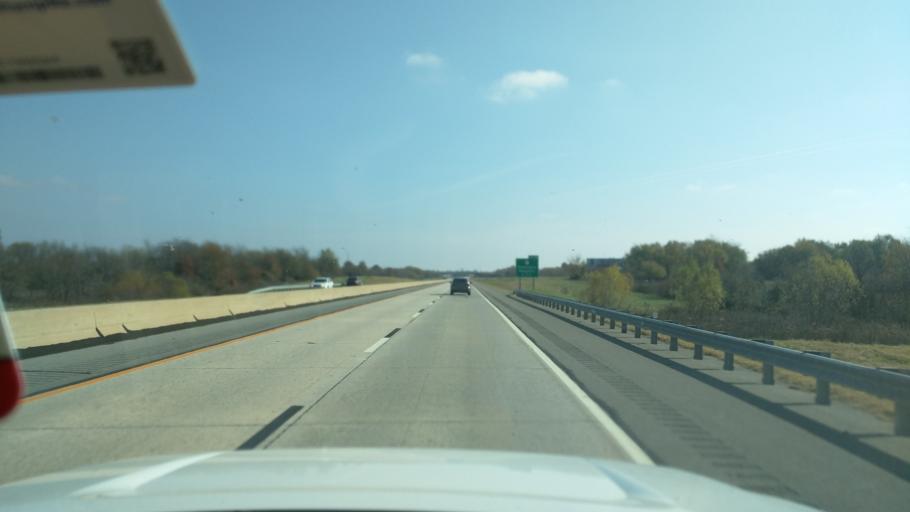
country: US
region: Oklahoma
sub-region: Wagoner County
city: Wagoner
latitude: 35.8589
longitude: -95.4411
